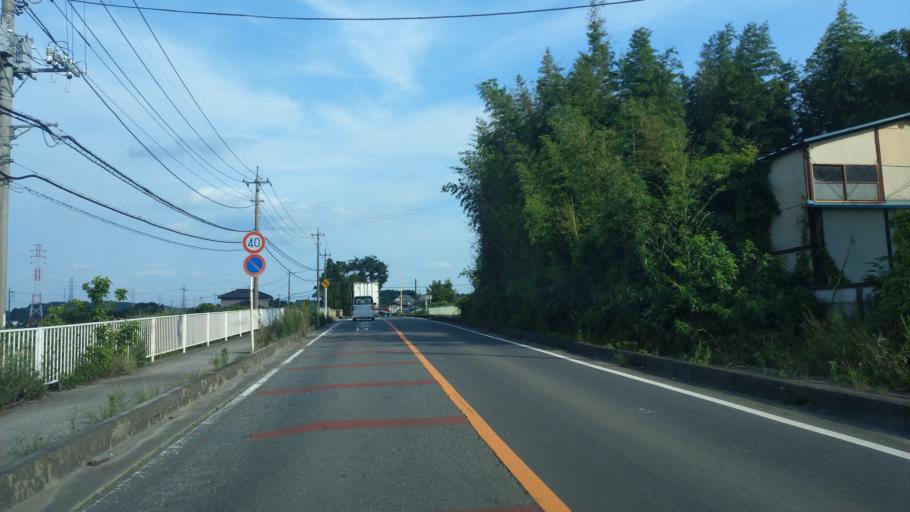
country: JP
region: Saitama
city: Ogawa
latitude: 36.0949
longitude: 139.2750
